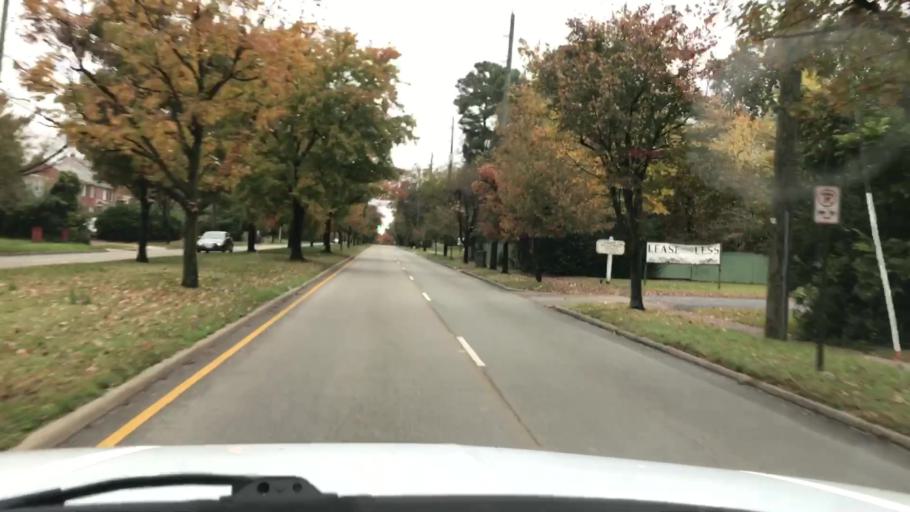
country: US
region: Virginia
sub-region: City of Richmond
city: Richmond
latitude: 37.5756
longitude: -77.4457
